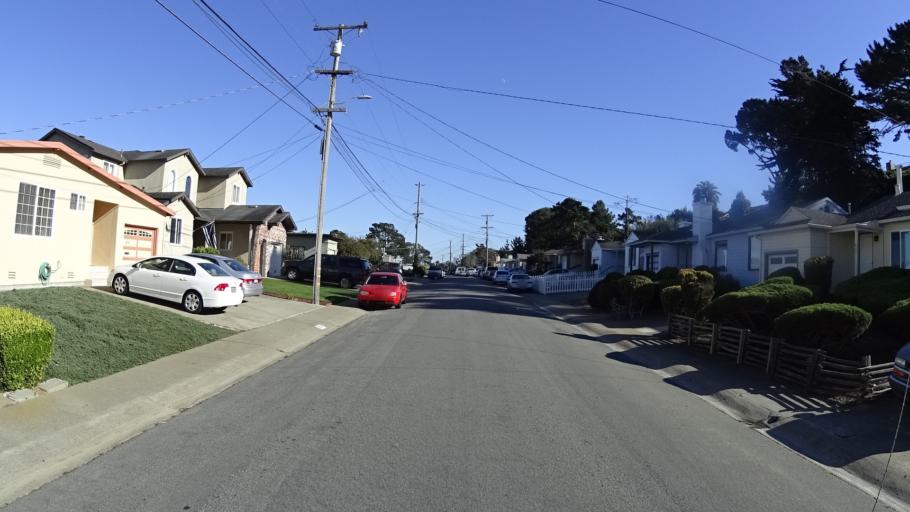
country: US
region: California
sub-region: San Mateo County
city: Broadmoor
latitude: 37.6916
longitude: -122.4861
